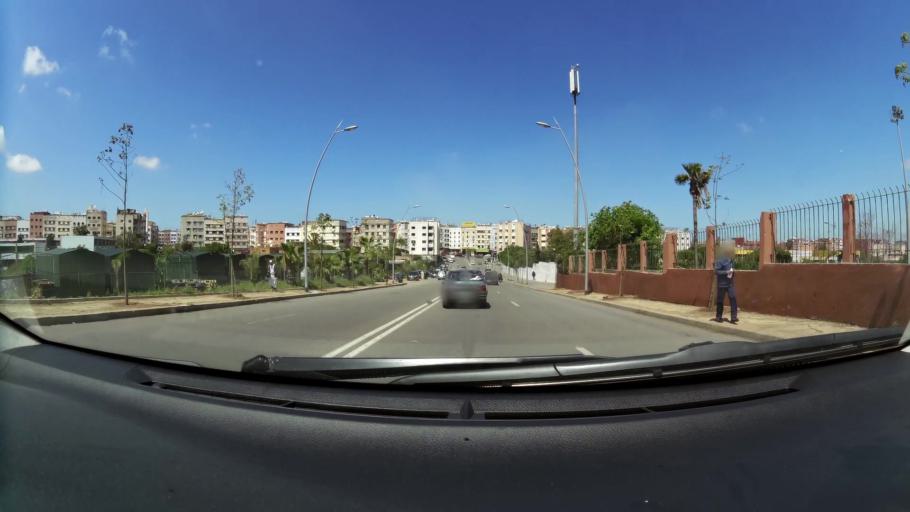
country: MA
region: Grand Casablanca
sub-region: Casablanca
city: Casablanca
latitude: 33.5619
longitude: -7.5877
